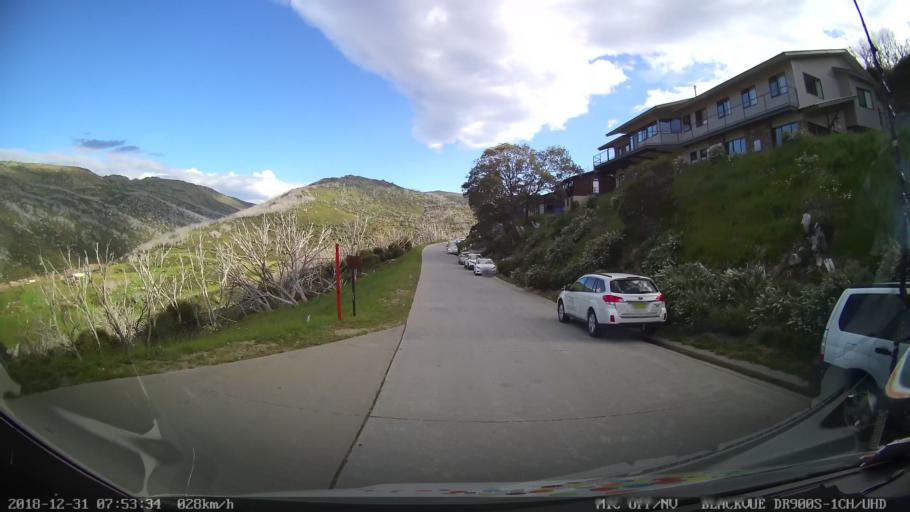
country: AU
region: New South Wales
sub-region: Snowy River
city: Jindabyne
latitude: -36.3801
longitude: 148.3738
